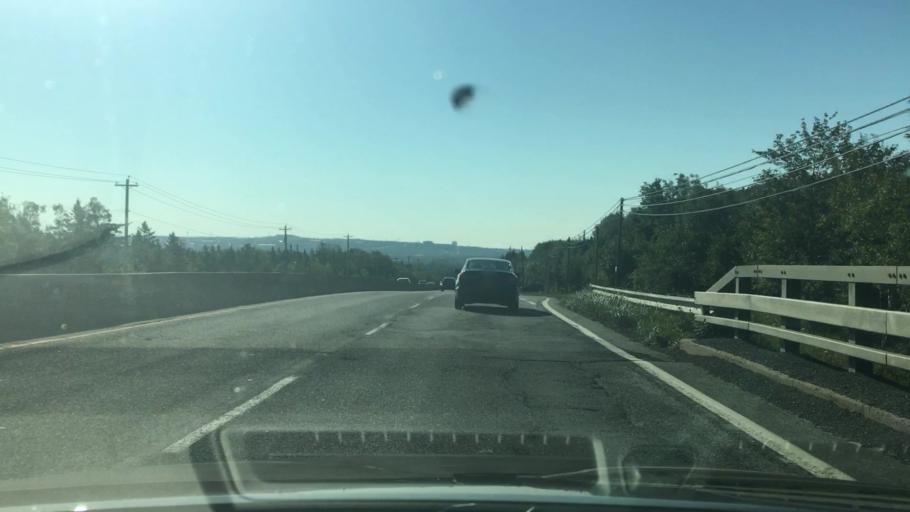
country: CA
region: Nova Scotia
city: Dartmouth
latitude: 44.7135
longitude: -63.6300
